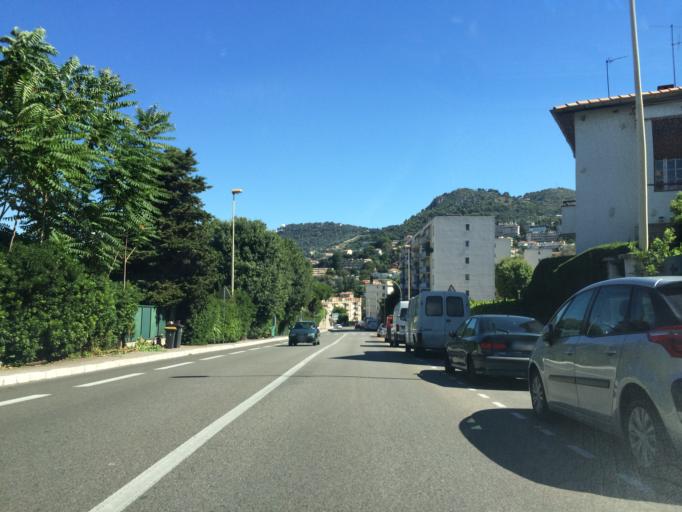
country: FR
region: Provence-Alpes-Cote d'Azur
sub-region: Departement des Alpes-Maritimes
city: Villefranche-sur-Mer
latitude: 43.6999
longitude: 7.2940
